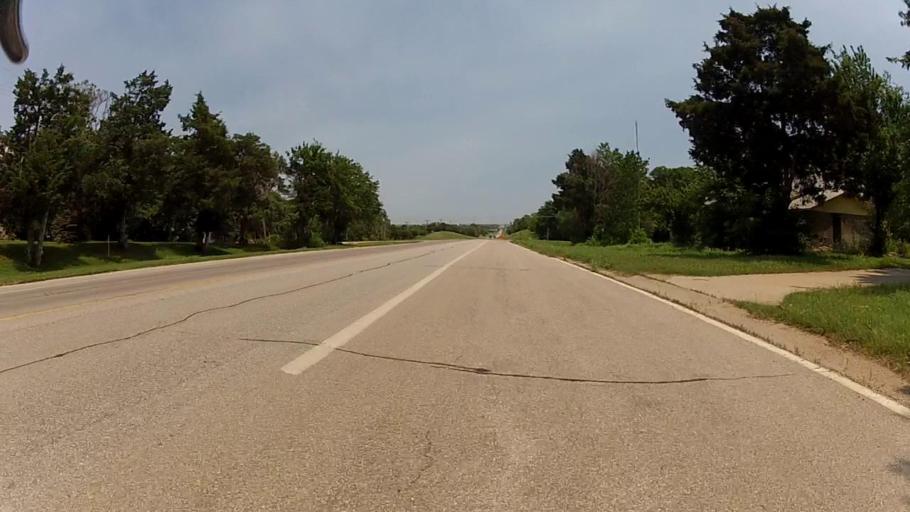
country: US
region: Kansas
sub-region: Cowley County
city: Arkansas City
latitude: 37.0565
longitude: -97.0769
